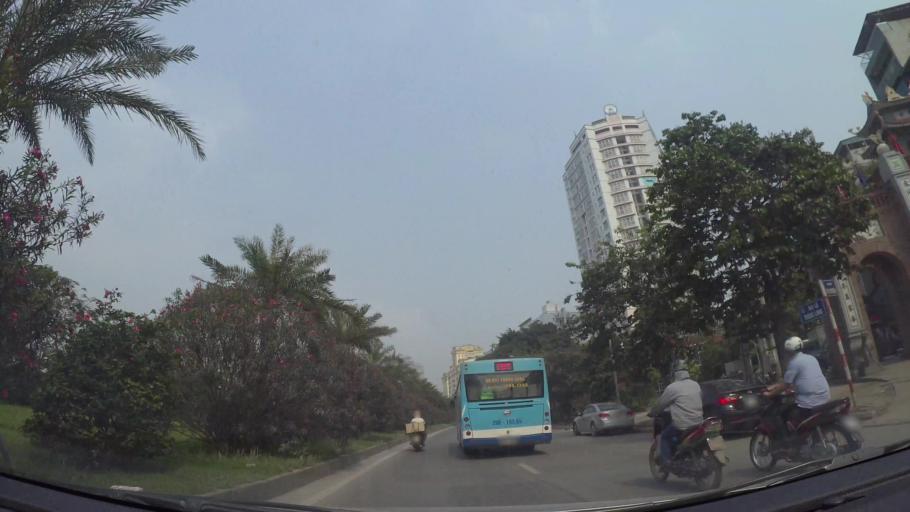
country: VN
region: Ha Noi
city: Thanh Xuan
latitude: 21.0035
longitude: 105.7794
